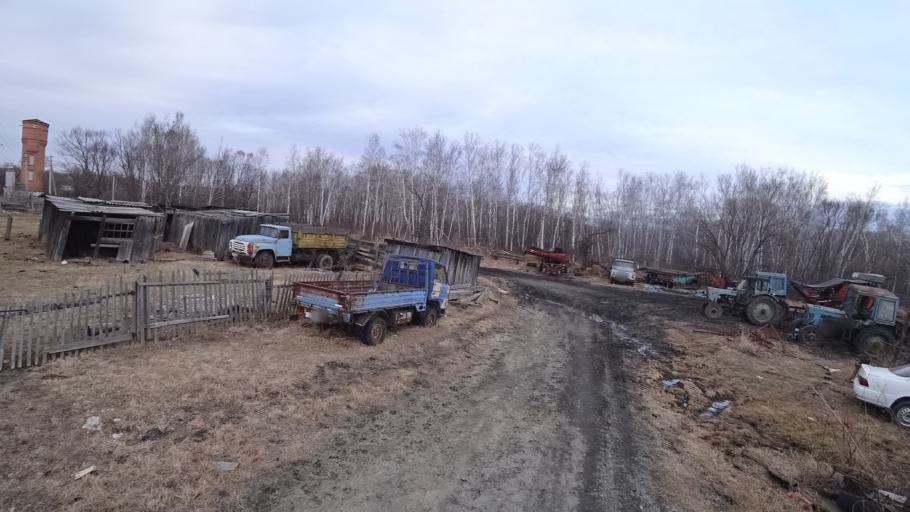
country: RU
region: Amur
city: Bureya
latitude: 50.0154
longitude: 129.7701
